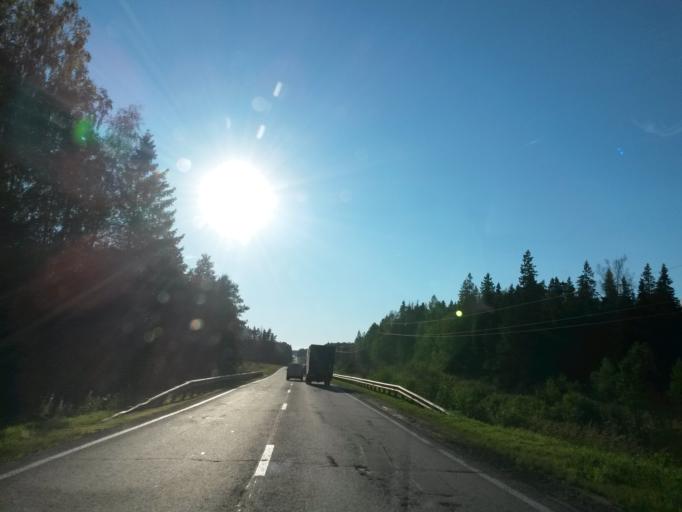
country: RU
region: Jaroslavl
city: Gavrilov-Yam
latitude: 57.2660
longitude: 40.0004
